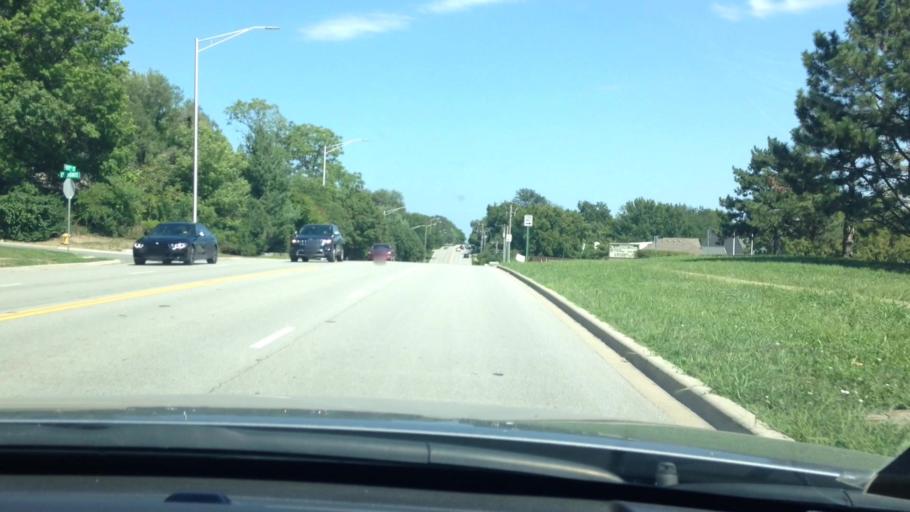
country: US
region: Kansas
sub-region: Johnson County
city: Leawood
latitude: 38.9422
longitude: -94.6364
